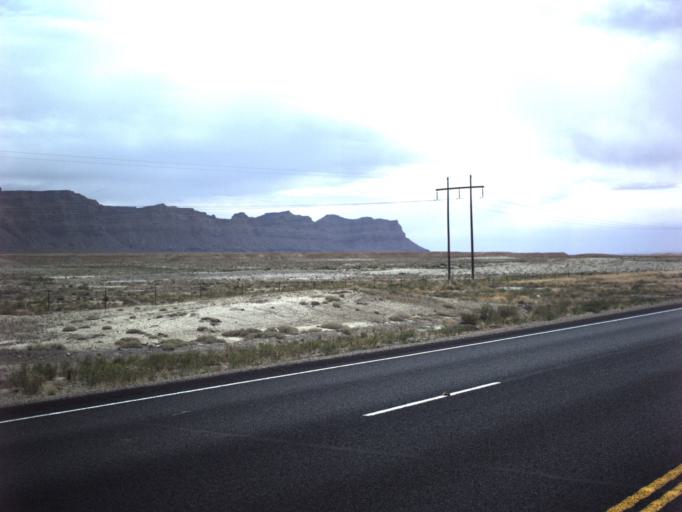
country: US
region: Utah
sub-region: Carbon County
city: East Carbon City
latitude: 39.1738
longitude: -110.3384
